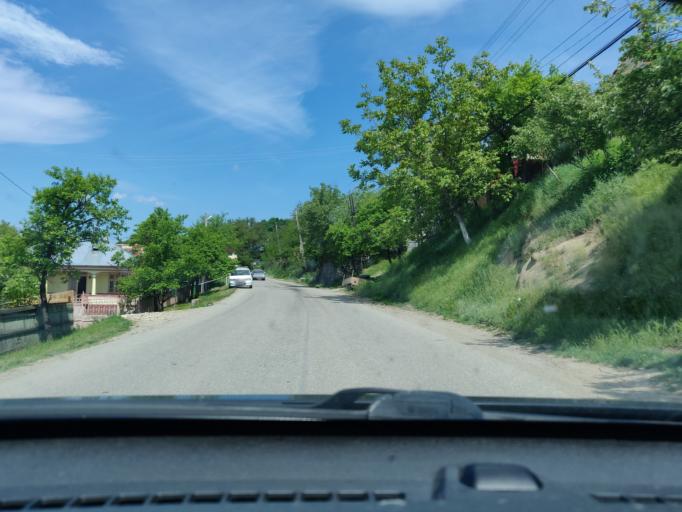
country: RO
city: Vizantea-Manastireasca
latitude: 45.9578
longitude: 26.8282
